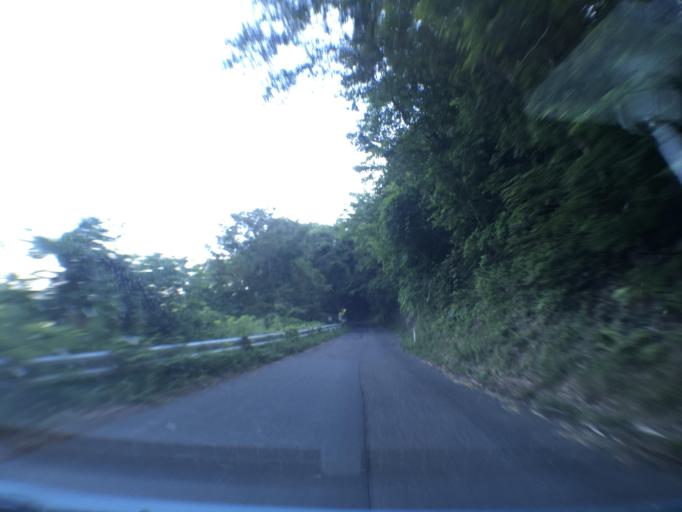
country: JP
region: Miyagi
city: Wakuya
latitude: 38.6244
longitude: 141.2905
